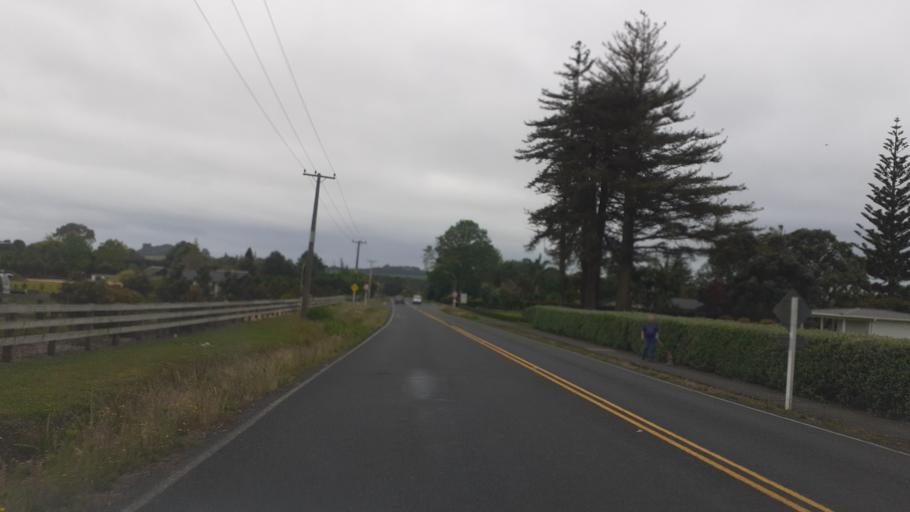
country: NZ
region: Northland
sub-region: Far North District
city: Kerikeri
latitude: -35.2091
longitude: 173.9637
